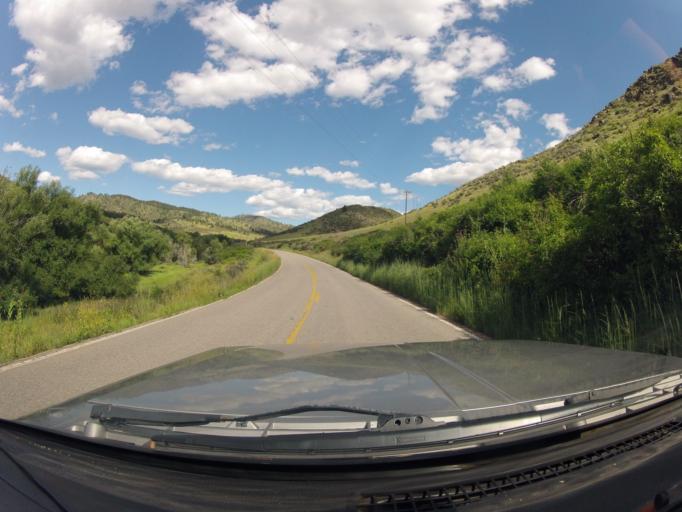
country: US
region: Colorado
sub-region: Larimer County
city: Laporte
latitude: 40.5368
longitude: -105.2732
